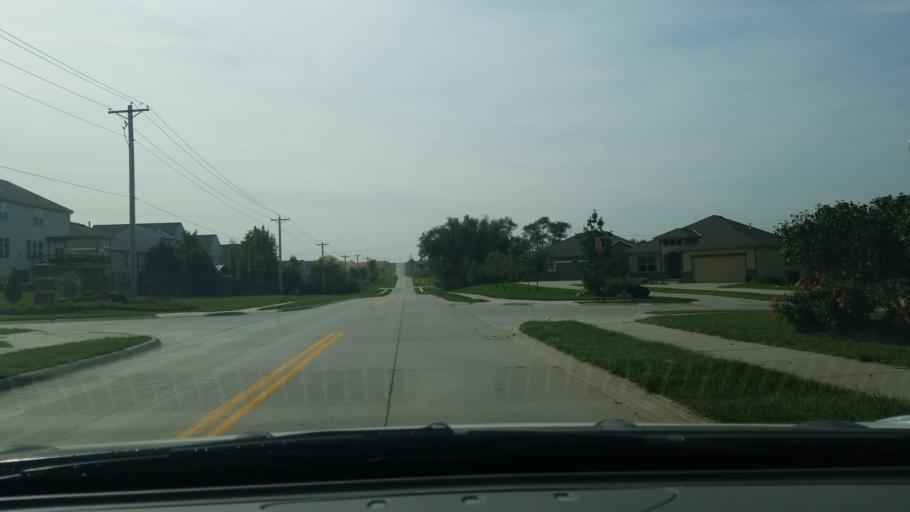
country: US
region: Nebraska
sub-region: Sarpy County
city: Papillion
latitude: 41.1289
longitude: -96.0621
